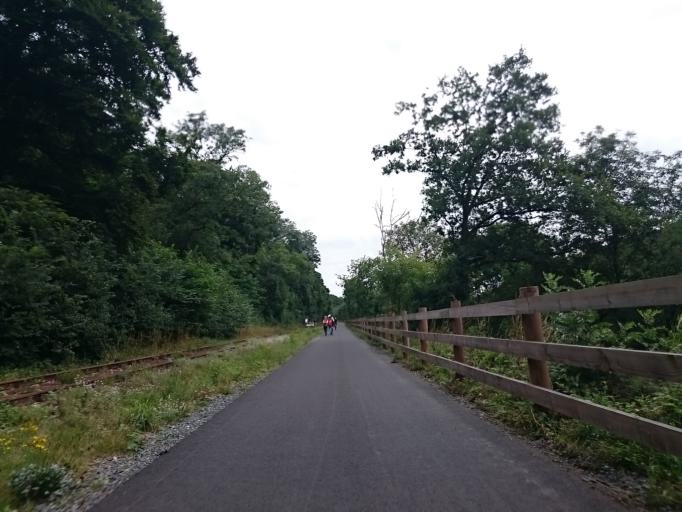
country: FR
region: Lower Normandy
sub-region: Departement du Calvados
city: Clinchamps-sur-Orne
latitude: 49.0718
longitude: -0.4318
